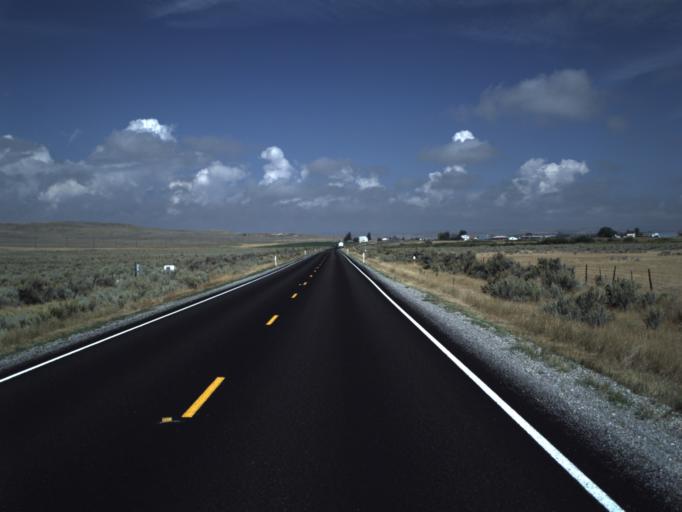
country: US
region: Utah
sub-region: Rich County
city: Randolph
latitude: 41.5893
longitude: -111.1704
